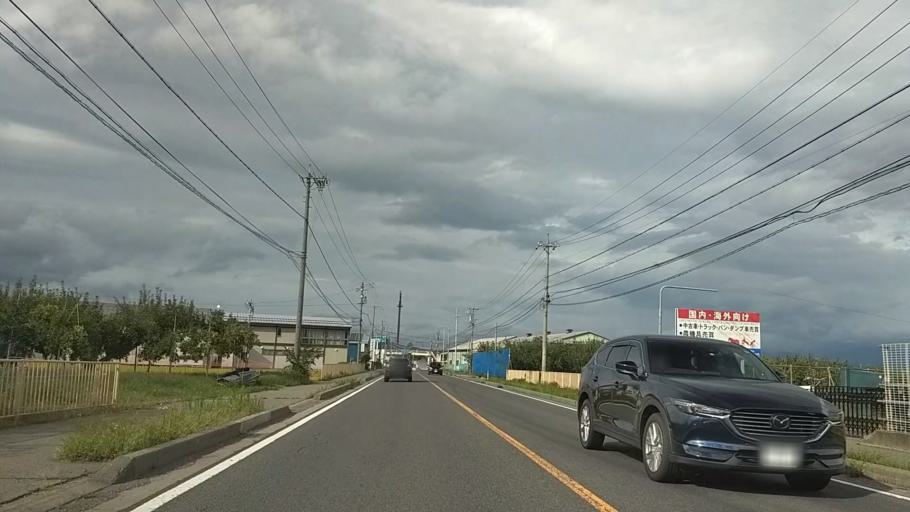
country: JP
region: Nagano
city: Suzaka
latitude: 36.6730
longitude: 138.2662
